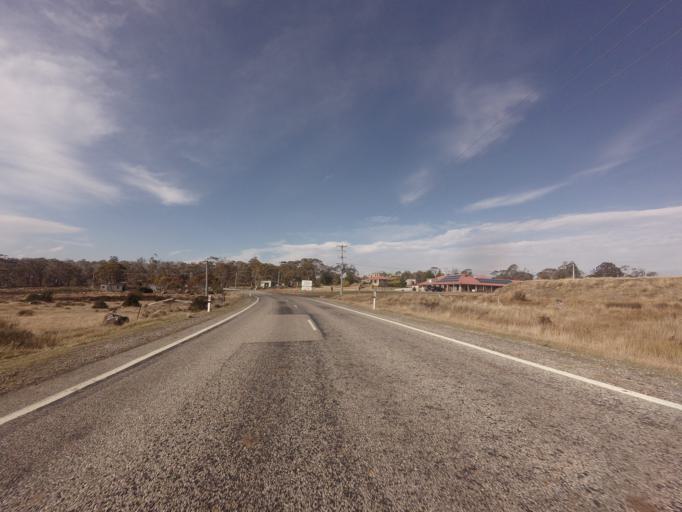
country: AU
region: Tasmania
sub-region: Meander Valley
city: Deloraine
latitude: -41.9930
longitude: 146.7051
